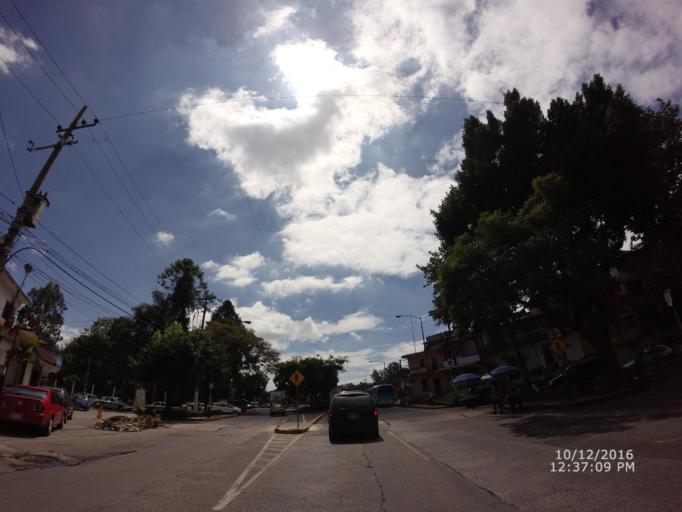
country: MX
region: Veracruz
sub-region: Xalapa
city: Xalapa de Enriquez
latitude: 19.5264
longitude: -96.9343
